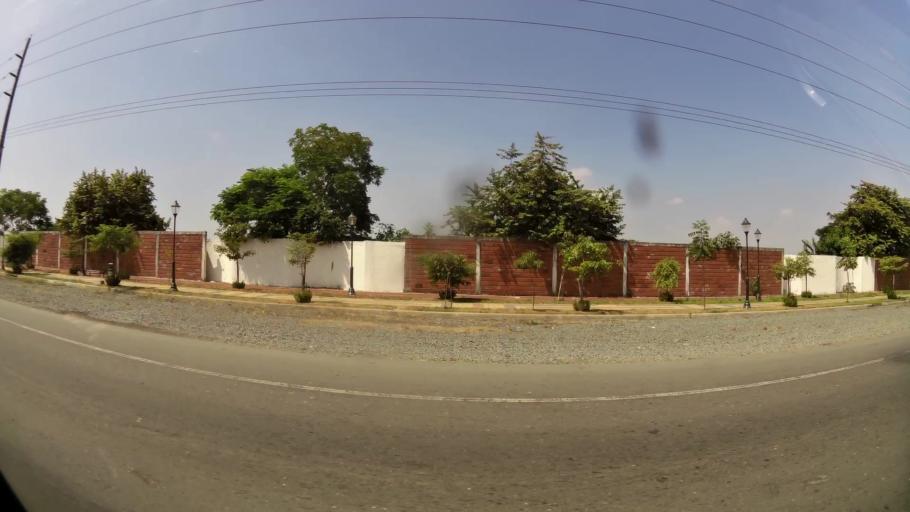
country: EC
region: Guayas
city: Eloy Alfaro
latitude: -2.0680
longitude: -79.8729
